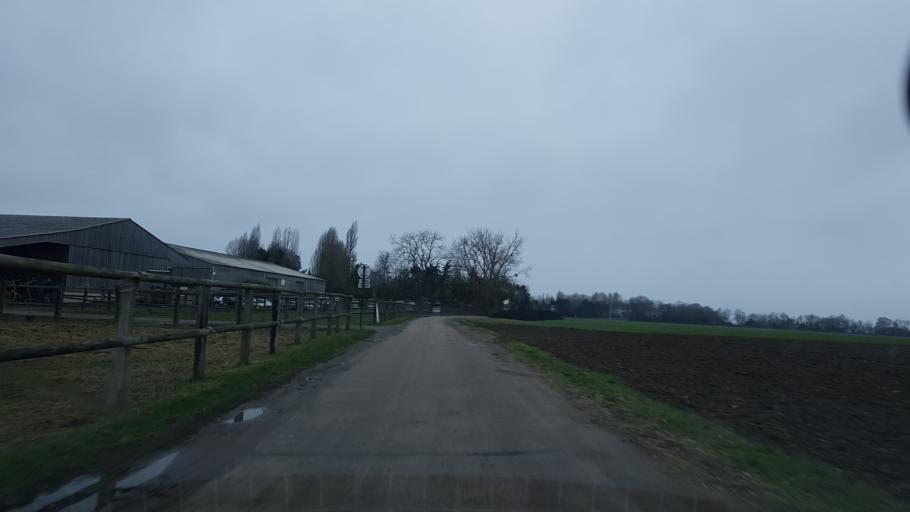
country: FR
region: Ile-de-France
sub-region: Departement de l'Essonne
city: Limours
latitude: 48.6543
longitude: 2.0969
